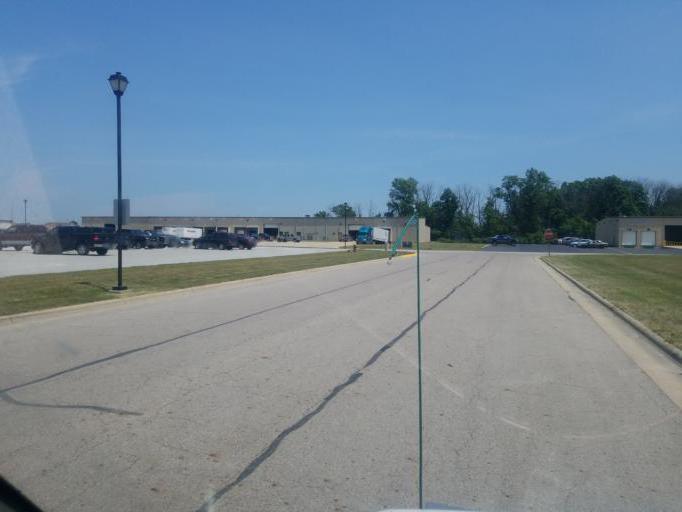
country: US
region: Ohio
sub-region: Shelby County
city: Fort Loramie
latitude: 40.3390
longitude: -84.3717
